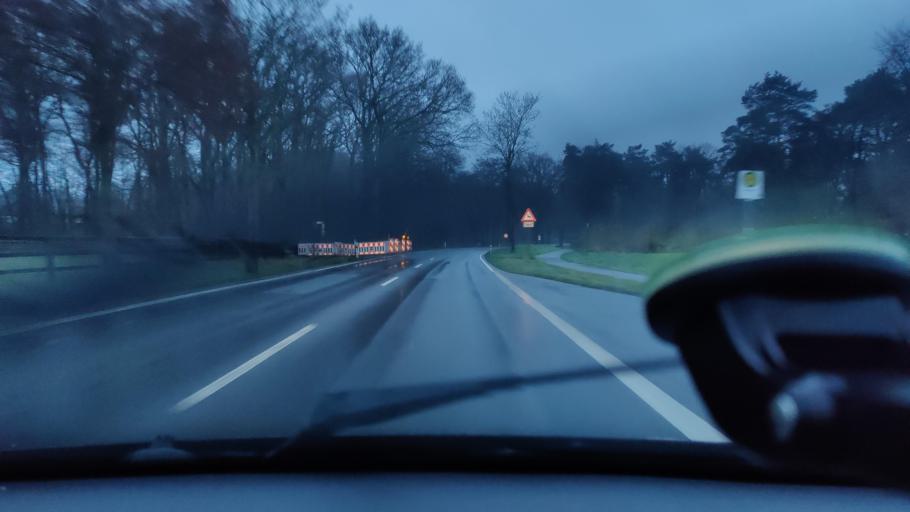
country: DE
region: North Rhine-Westphalia
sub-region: Regierungsbezirk Dusseldorf
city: Sonsbeck
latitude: 51.5954
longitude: 6.3847
